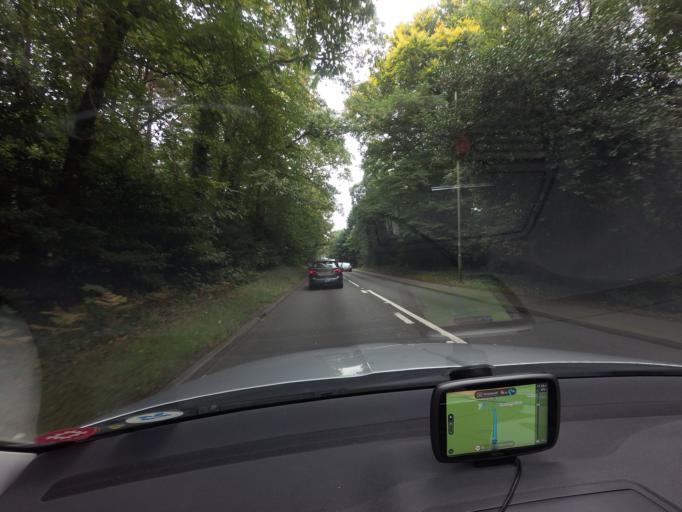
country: GB
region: England
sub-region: Surrey
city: Byfleet
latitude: 51.3371
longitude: -0.4428
